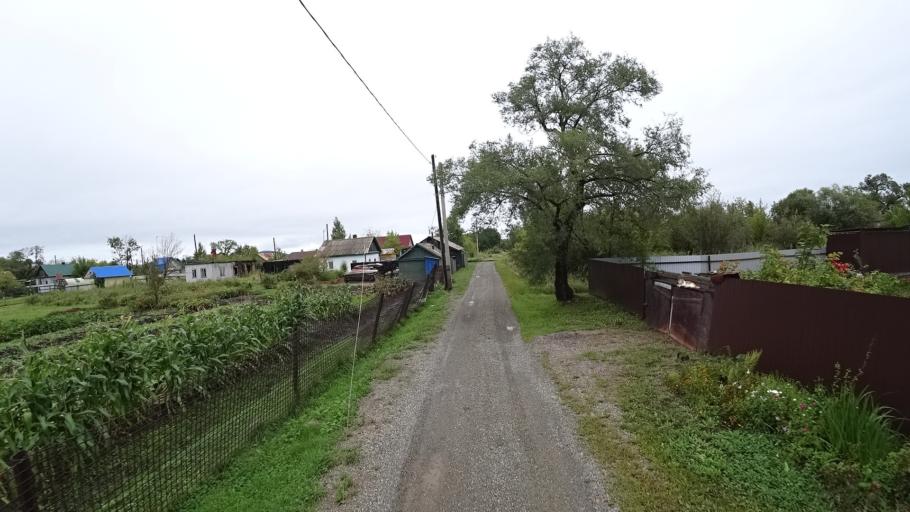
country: RU
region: Primorskiy
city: Monastyrishche
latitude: 44.2106
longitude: 132.4335
